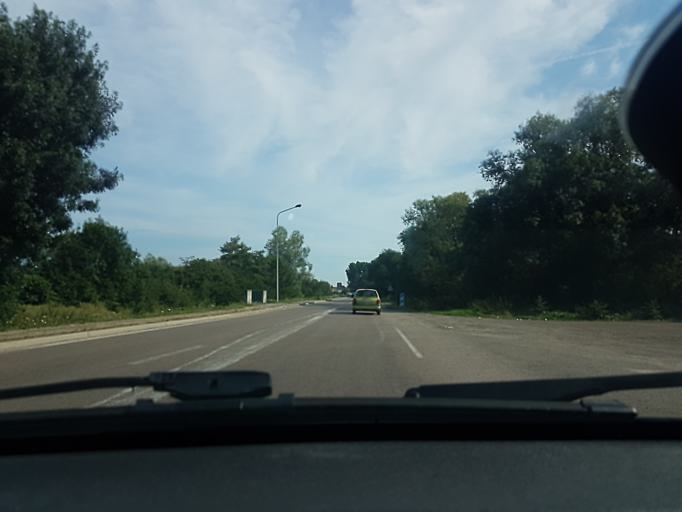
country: FR
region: Bourgogne
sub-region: Departement de Saone-et-Loire
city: Saint-Marcel
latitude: 46.7625
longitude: 4.8931
